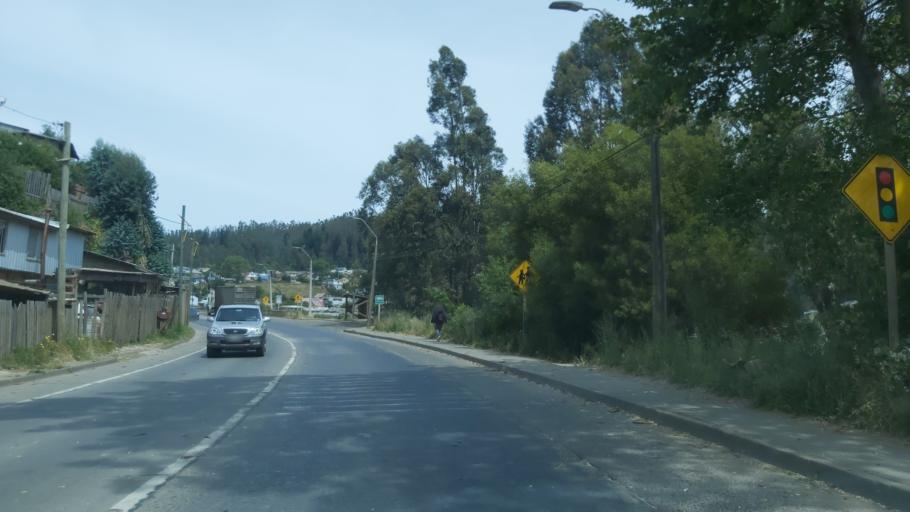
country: CL
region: Maule
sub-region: Provincia de Talca
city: Constitucion
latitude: -35.3401
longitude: -72.4204
